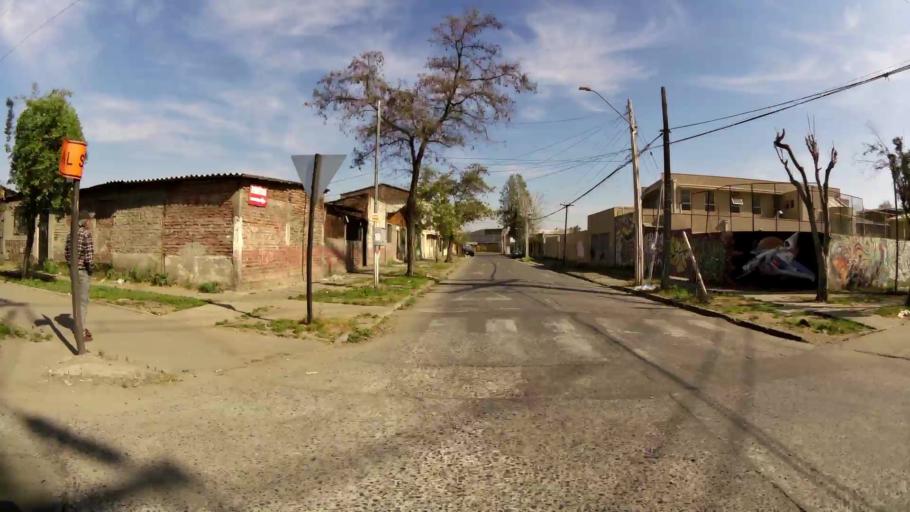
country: CL
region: Santiago Metropolitan
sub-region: Provincia de Santiago
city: Santiago
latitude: -33.4027
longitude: -70.6295
